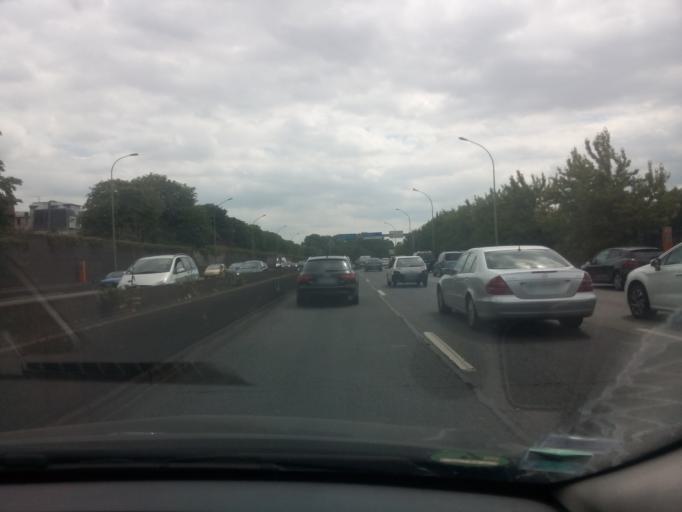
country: FR
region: Ile-de-France
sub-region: Departement du Val-de-Marne
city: Saint-Mande
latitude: 48.8380
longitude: 2.4128
